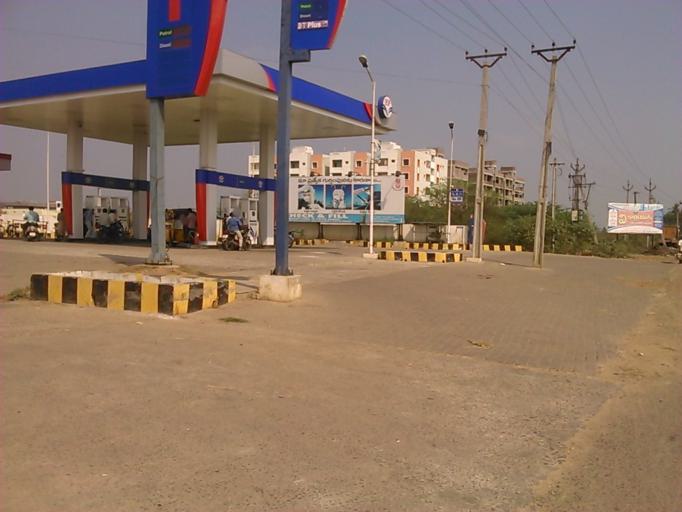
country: IN
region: Andhra Pradesh
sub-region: Guntur
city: Bhattiprolu
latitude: 16.2377
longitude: 80.6636
